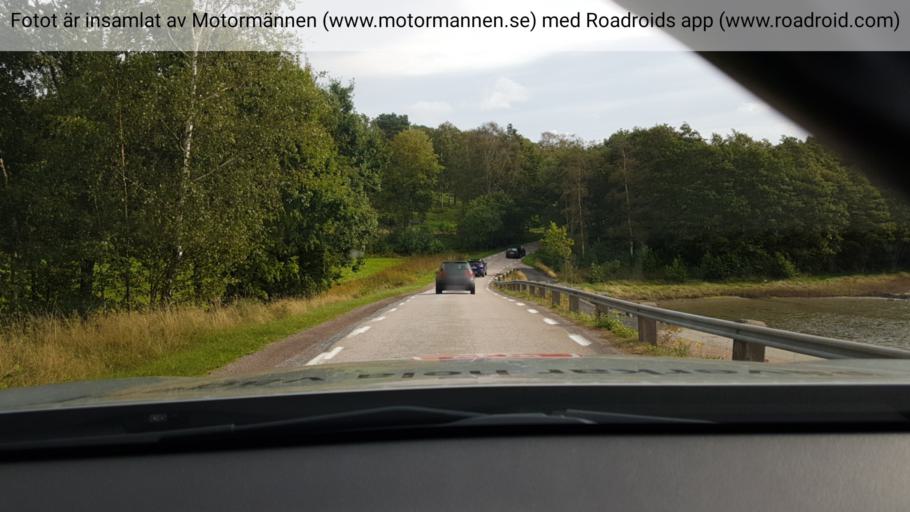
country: SE
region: Vaestra Goetaland
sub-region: Lysekils Kommun
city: Lysekil
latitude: 58.2394
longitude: 11.5473
